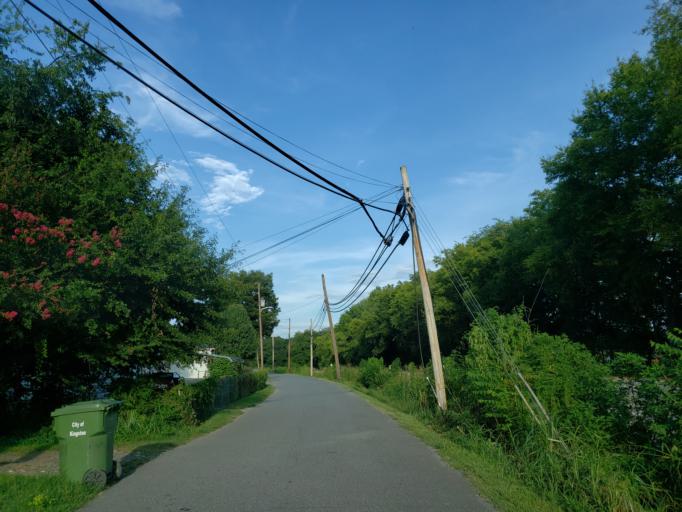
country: US
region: Georgia
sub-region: Bartow County
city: Euharlee
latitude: 34.2360
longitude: -84.9397
